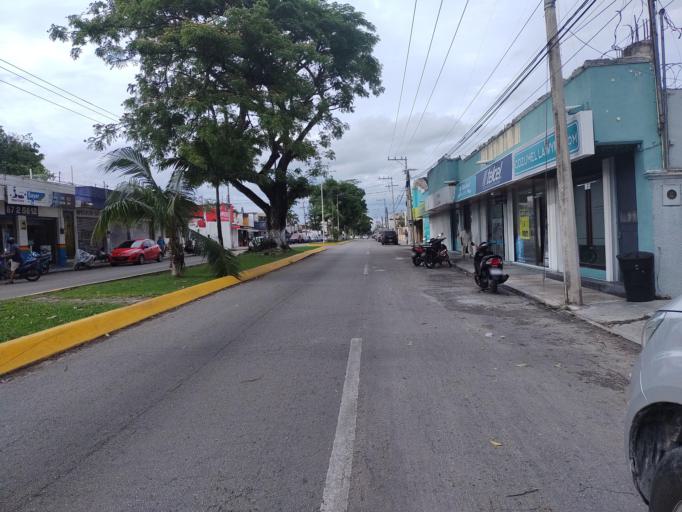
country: MX
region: Quintana Roo
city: San Miguel de Cozumel
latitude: 20.5023
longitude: -86.9491
